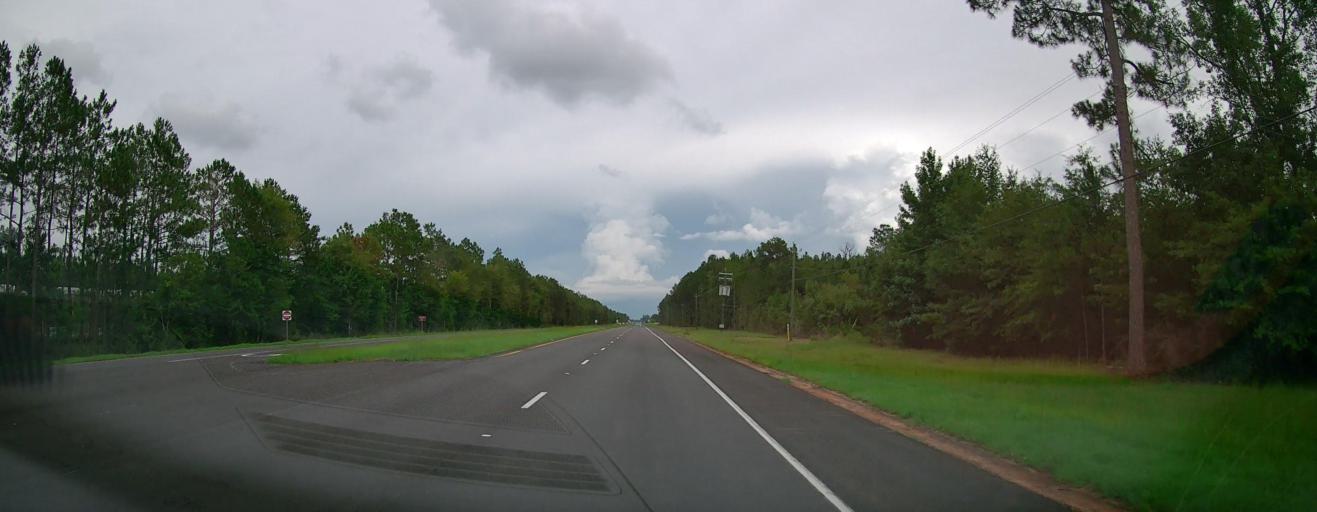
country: US
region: Georgia
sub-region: Wayne County
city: Jesup
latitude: 31.6493
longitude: -81.9837
